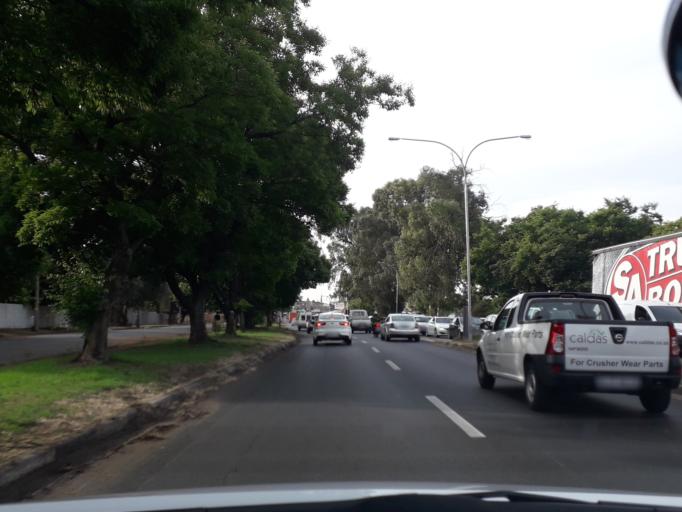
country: ZA
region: Gauteng
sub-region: City of Johannesburg Metropolitan Municipality
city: Modderfontein
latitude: -26.1523
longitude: 28.1598
